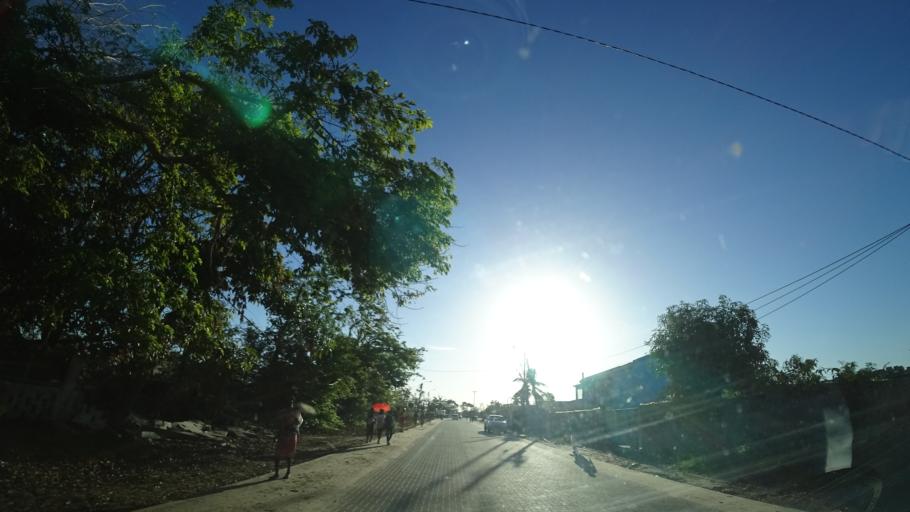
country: MZ
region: Sofala
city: Beira
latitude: -19.7433
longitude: 34.8406
